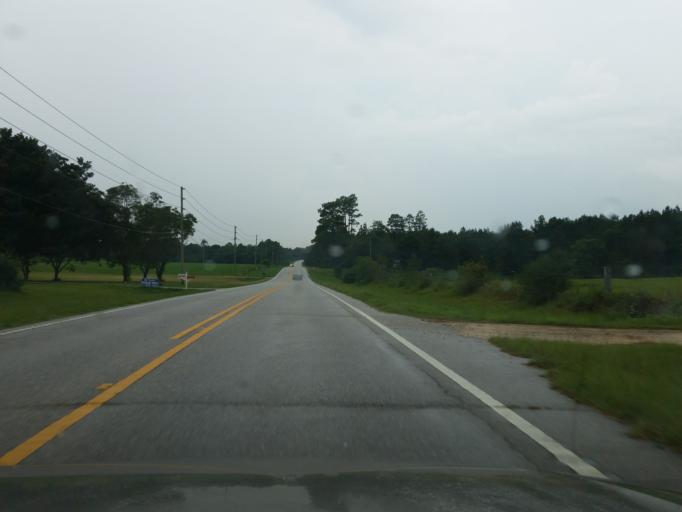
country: US
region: Alabama
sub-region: Baldwin County
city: Elberta
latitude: 30.5388
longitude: -87.5503
